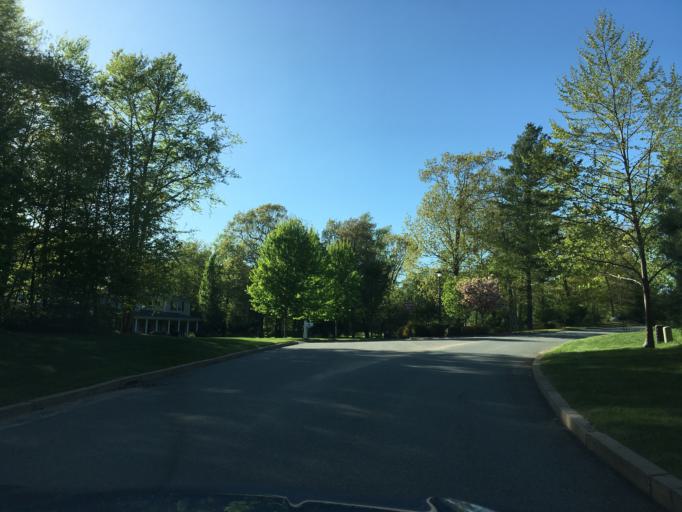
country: US
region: Rhode Island
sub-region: Washington County
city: Exeter
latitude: 41.6100
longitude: -71.5255
